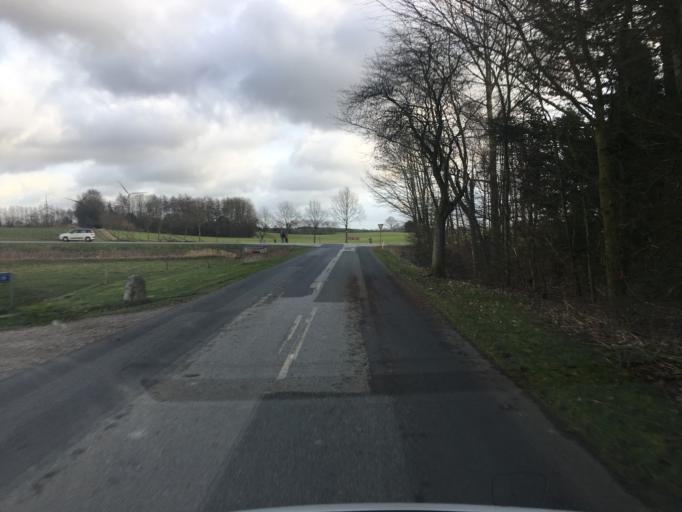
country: DE
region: Schleswig-Holstein
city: Wees
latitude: 54.8945
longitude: 9.4905
